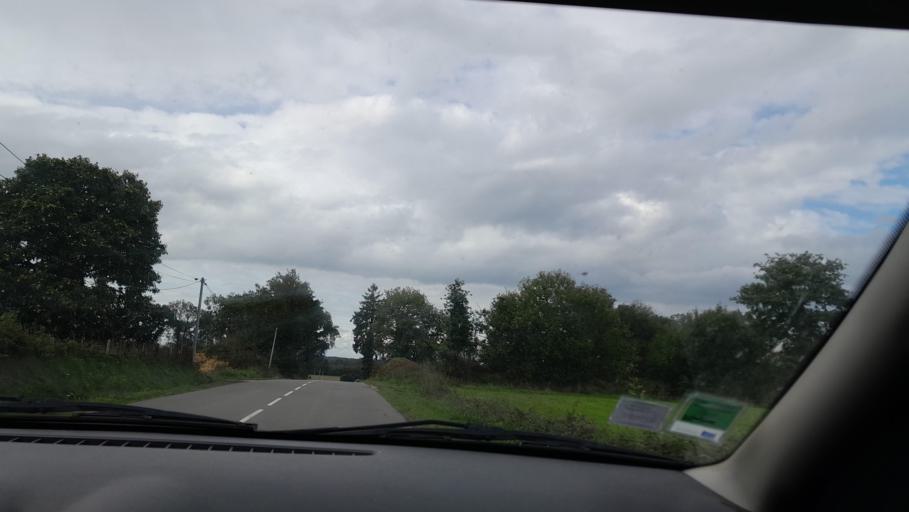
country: FR
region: Brittany
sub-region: Departement d'Ille-et-Vilaine
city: Argentre-du-Plessis
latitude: 48.0486
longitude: -1.0926
